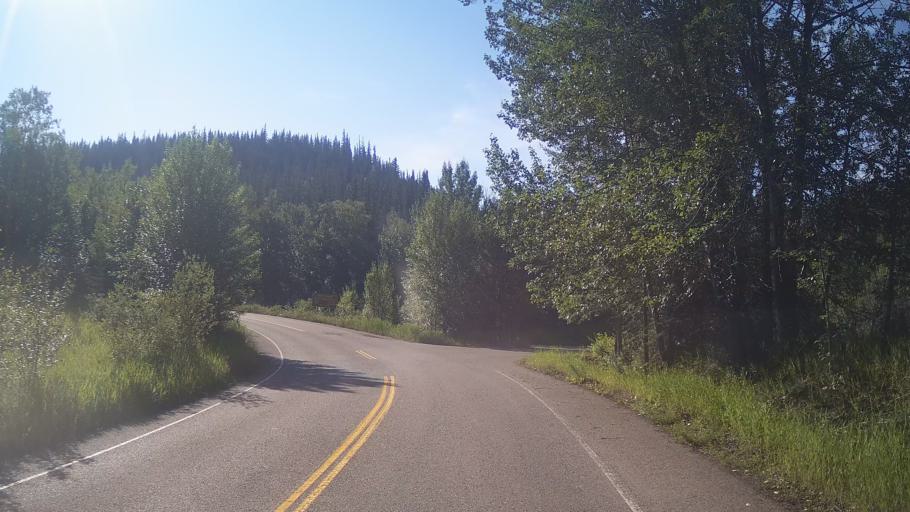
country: CA
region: Alberta
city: Jasper Park Lodge
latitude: 53.2045
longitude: -117.9269
